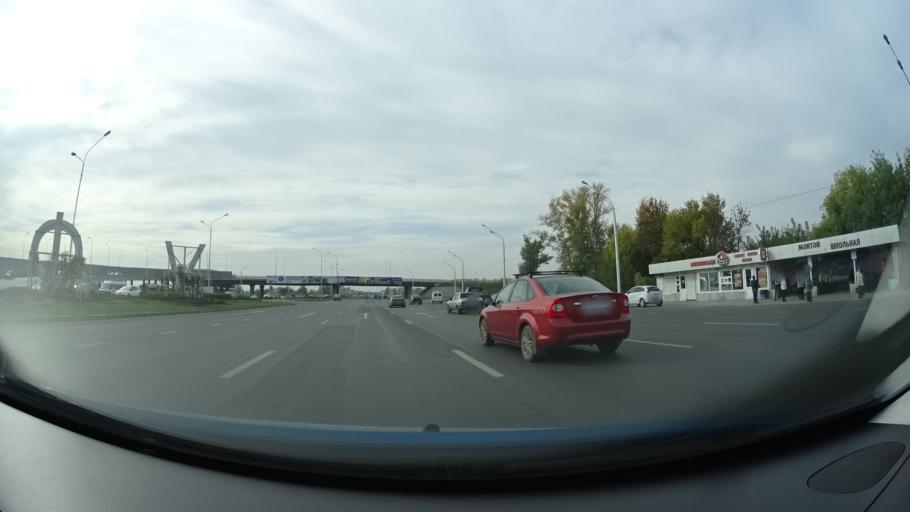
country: RU
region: Bashkortostan
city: Ufa
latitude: 54.7029
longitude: 55.9497
